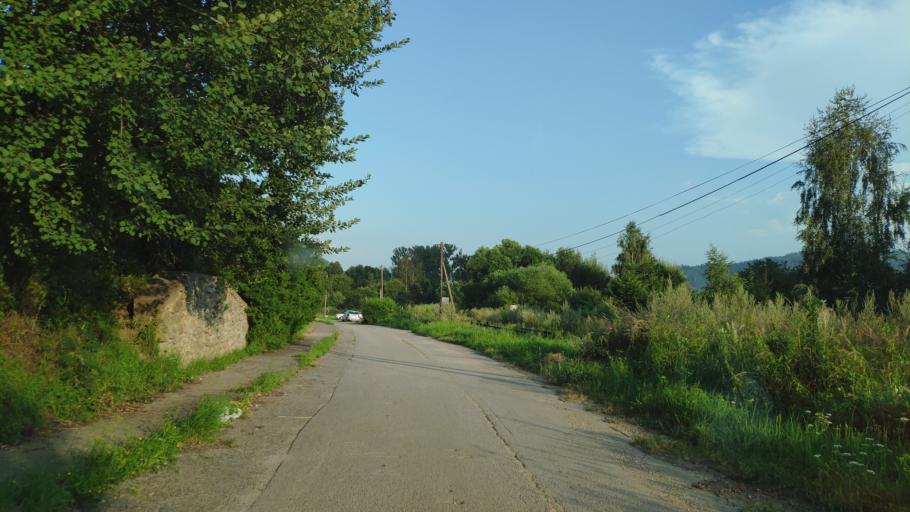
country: SK
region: Kosicky
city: Dobsina
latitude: 48.7205
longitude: 20.2743
